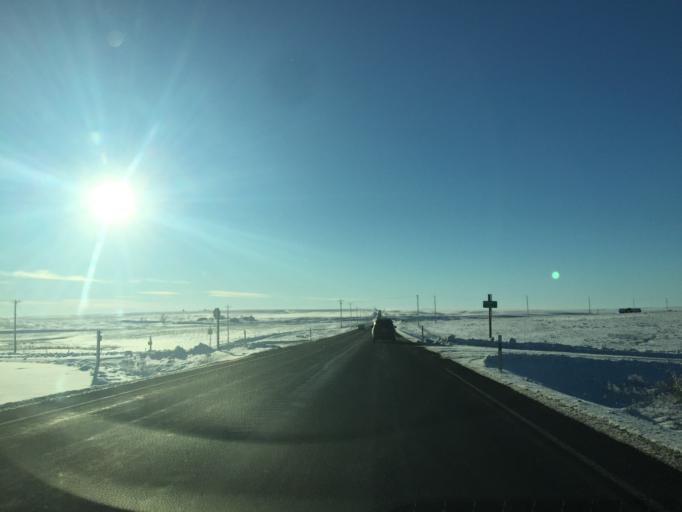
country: US
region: Washington
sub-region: Okanogan County
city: Coulee Dam
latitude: 47.7441
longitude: -118.8292
